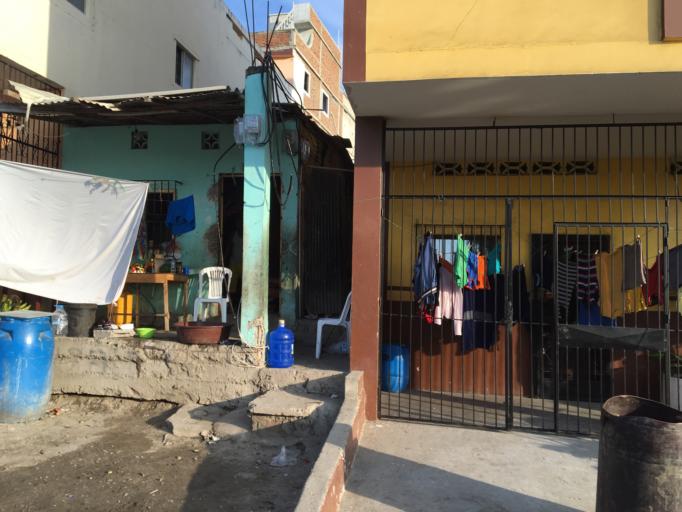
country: EC
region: Manabi
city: Manta
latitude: -0.9519
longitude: -80.7097
